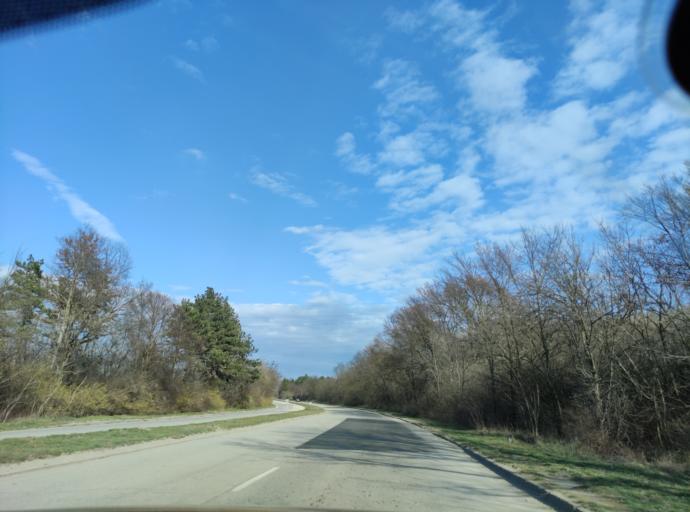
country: BG
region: Pleven
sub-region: Obshtina Dolna Mitropoliya
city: Dolna Mitropoliya
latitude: 43.4339
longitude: 24.5555
